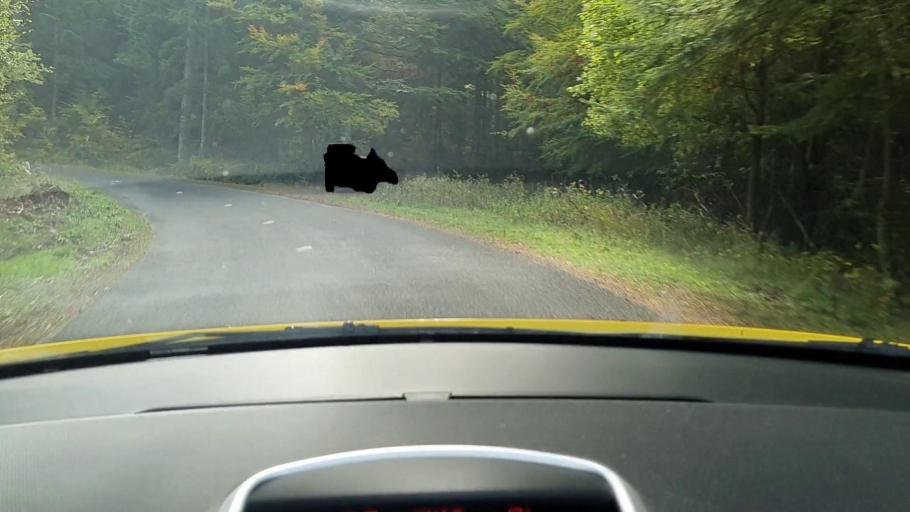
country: FR
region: Languedoc-Roussillon
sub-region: Departement du Gard
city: Valleraugue
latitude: 44.0766
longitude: 3.5630
